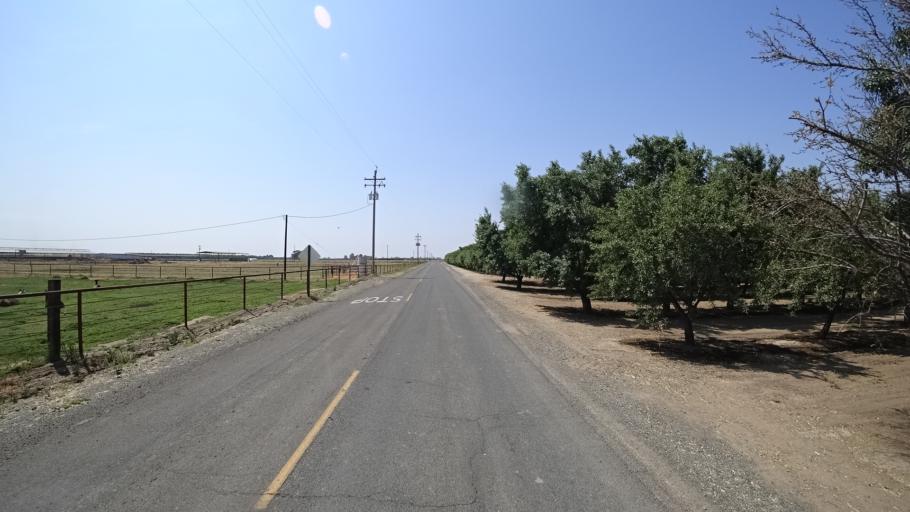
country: US
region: California
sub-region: Kings County
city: Armona
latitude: 36.3412
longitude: -119.7448
